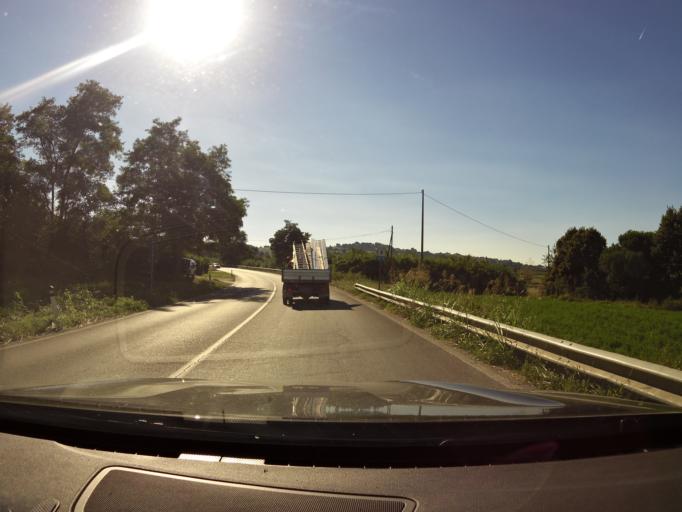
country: IT
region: The Marches
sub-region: Provincia di Ancona
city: Villa Musone
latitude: 43.4770
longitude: 13.5871
